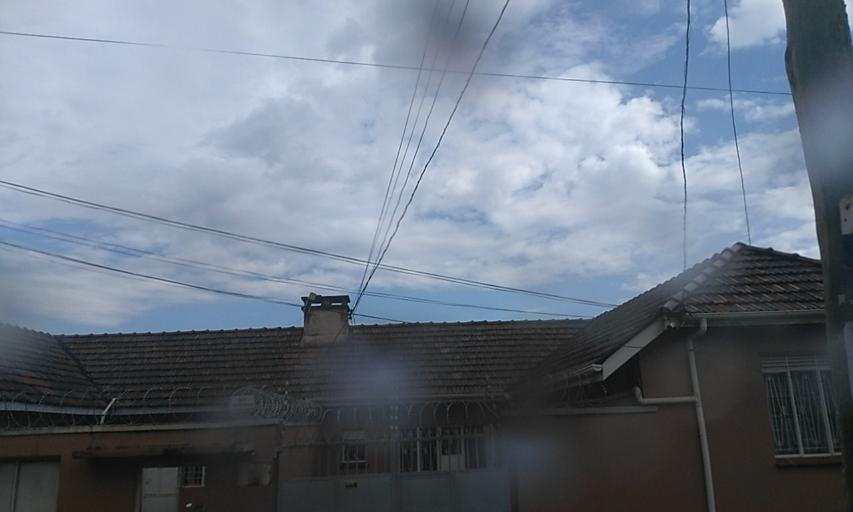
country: UG
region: Central Region
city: Kampala Central Division
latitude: 0.3425
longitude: 32.5934
